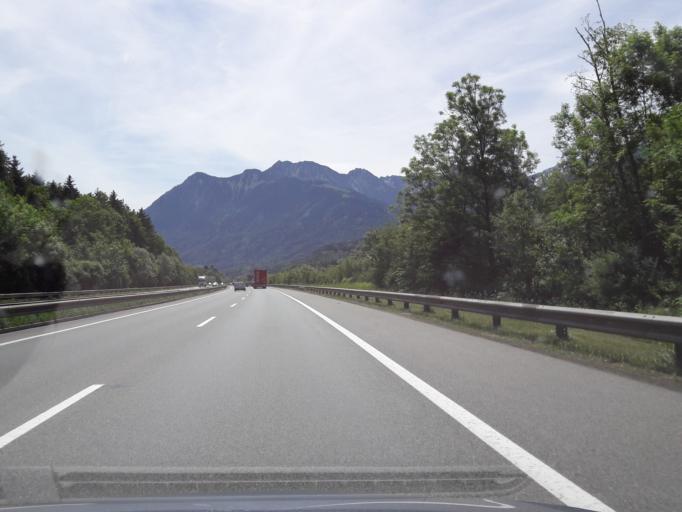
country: AT
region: Vorarlberg
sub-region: Politischer Bezirk Feldkirch
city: Satteins
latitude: 47.2152
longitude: 9.6590
